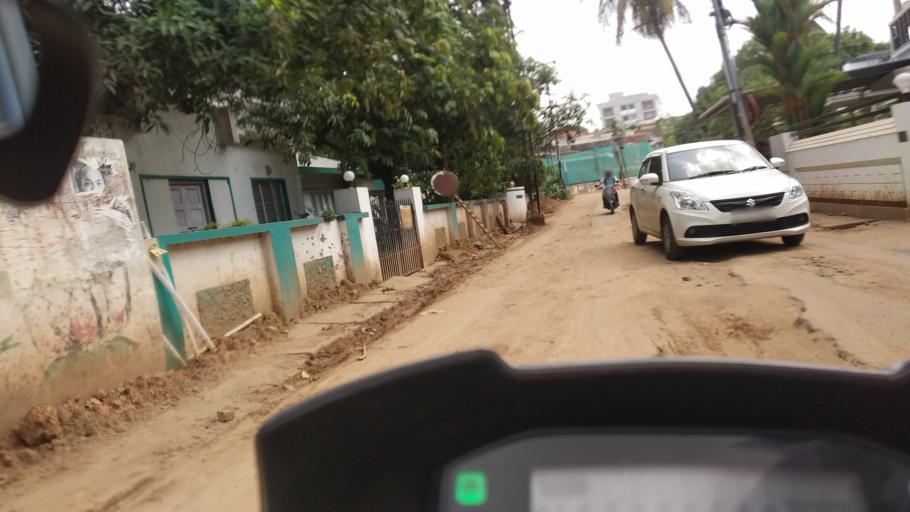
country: IN
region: Kerala
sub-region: Ernakulam
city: Cochin
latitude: 9.9911
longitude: 76.2917
